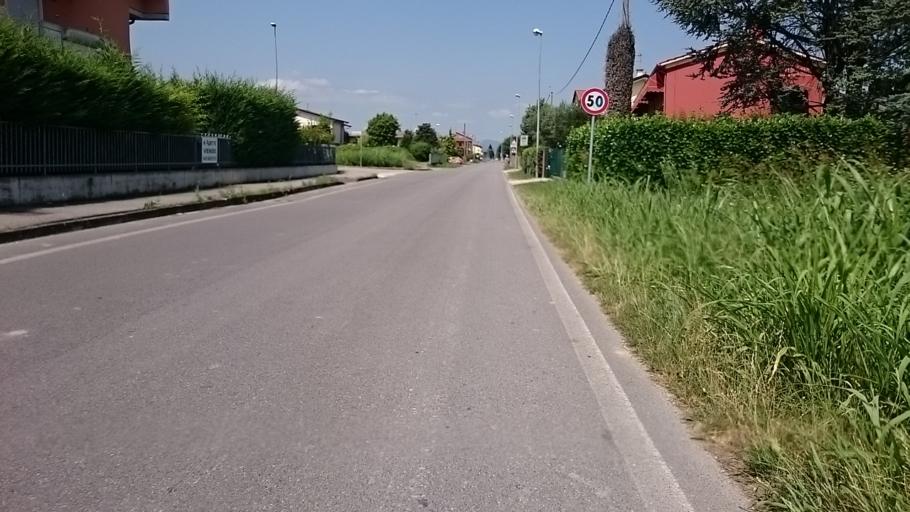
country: IT
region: Veneto
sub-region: Provincia di Padova
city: Masera di Padova
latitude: 45.3229
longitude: 11.8701
